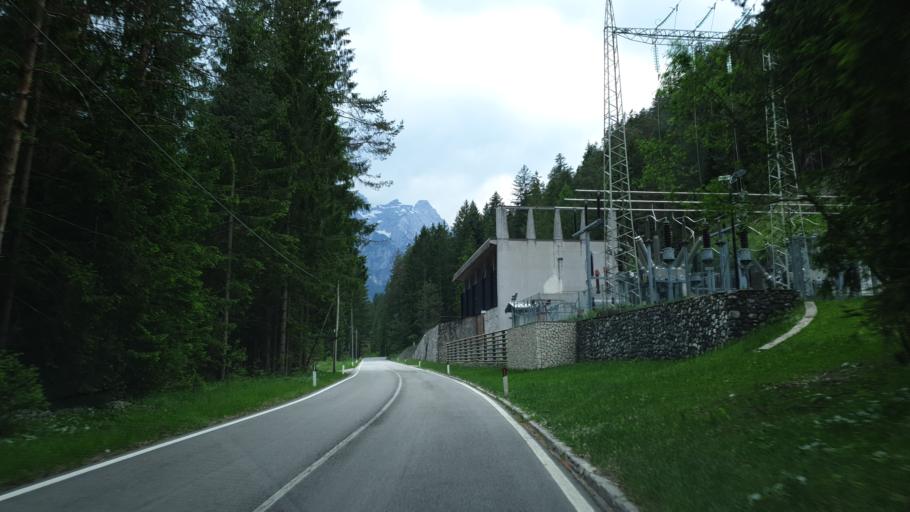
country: IT
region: Veneto
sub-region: Provincia di Belluno
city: Auronzo
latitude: 46.5621
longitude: 12.3437
